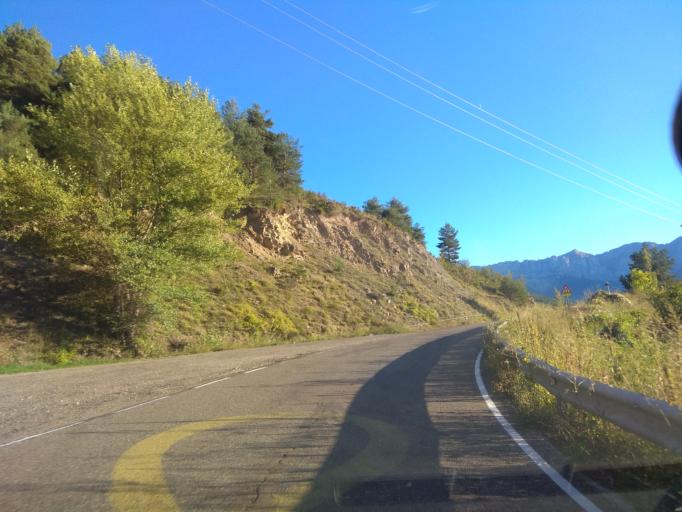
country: ES
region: Catalonia
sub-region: Provincia de Lleida
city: Lles de Cerdanya
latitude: 42.3544
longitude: 1.6897
